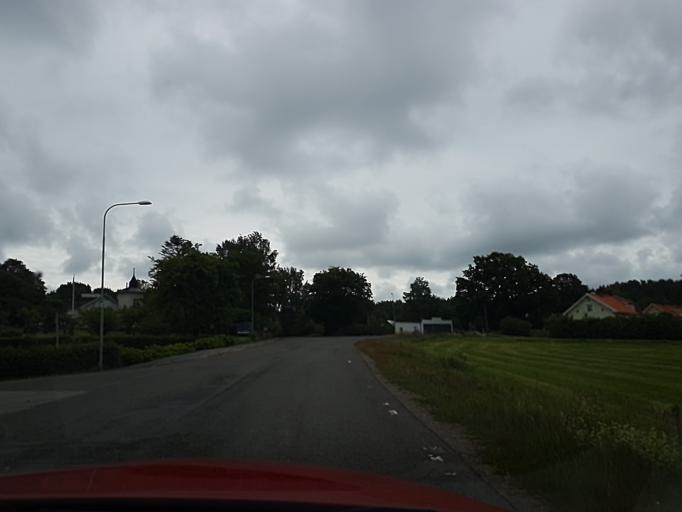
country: SE
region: Vaestra Goetaland
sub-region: Tidaholms Kommun
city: Olofstorp
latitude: 58.3048
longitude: 14.0957
